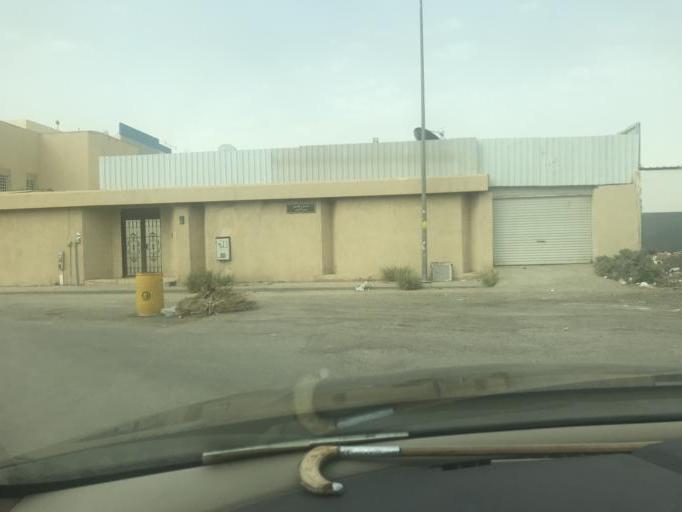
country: SA
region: Ar Riyad
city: Riyadh
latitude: 24.7324
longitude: 46.7887
